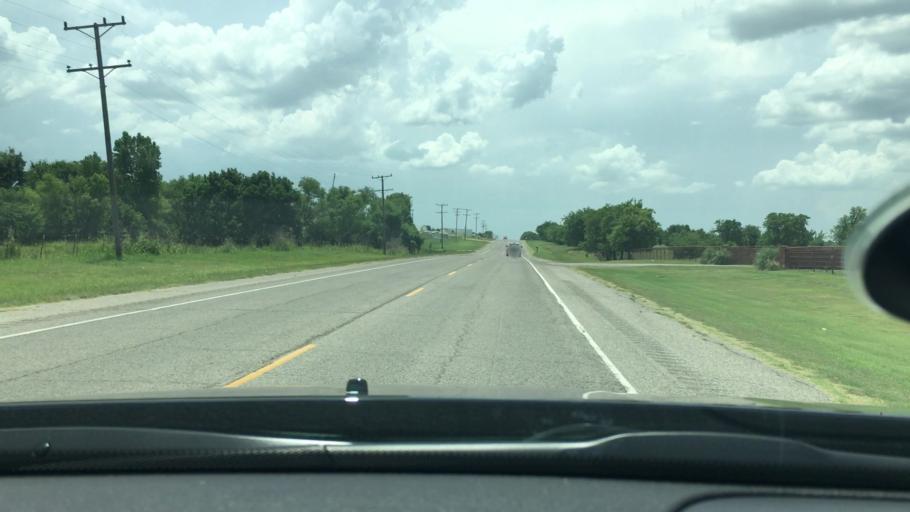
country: US
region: Oklahoma
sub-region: Love County
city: Marietta
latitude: 33.9548
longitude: -97.1263
